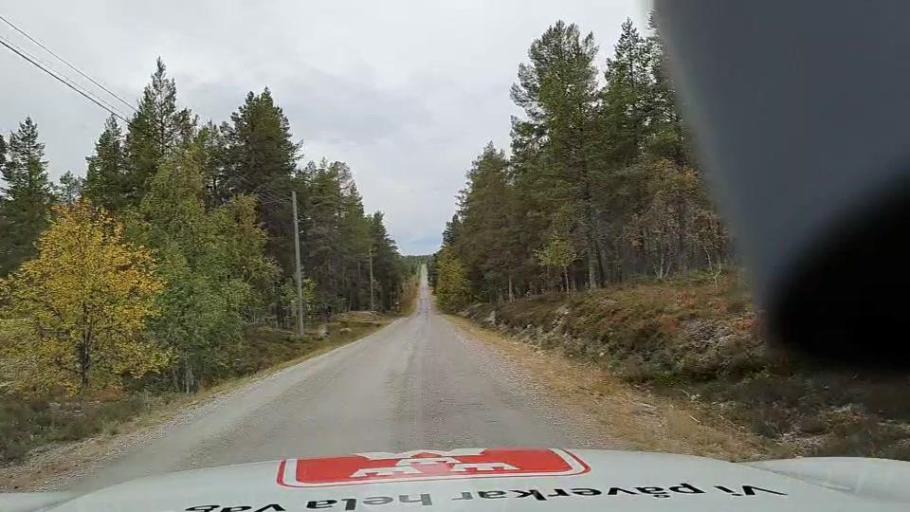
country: NO
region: Hedmark
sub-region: Engerdal
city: Engerdal
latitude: 62.0982
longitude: 12.8436
